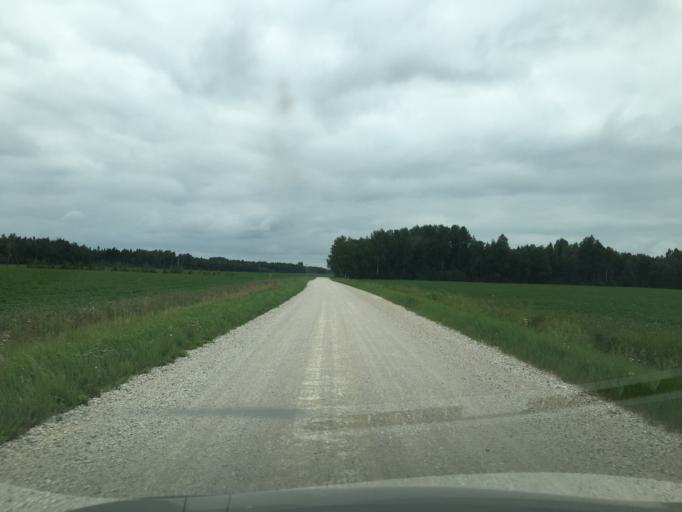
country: EE
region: Raplamaa
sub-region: Jaervakandi vald
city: Jarvakandi
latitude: 58.7957
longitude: 24.9592
